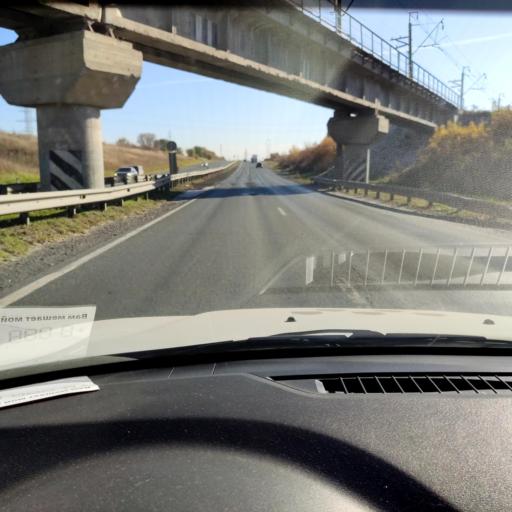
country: RU
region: Samara
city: Tol'yatti
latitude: 53.5690
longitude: 49.4820
